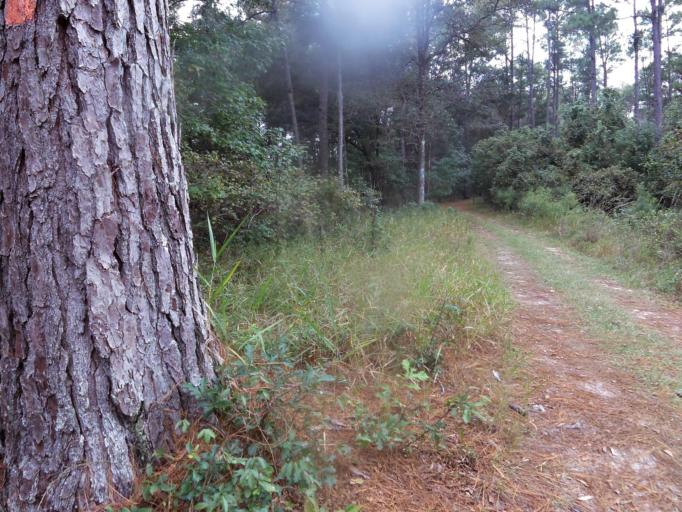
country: US
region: Florida
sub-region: Clay County
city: Keystone Heights
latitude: 29.8281
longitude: -81.9456
